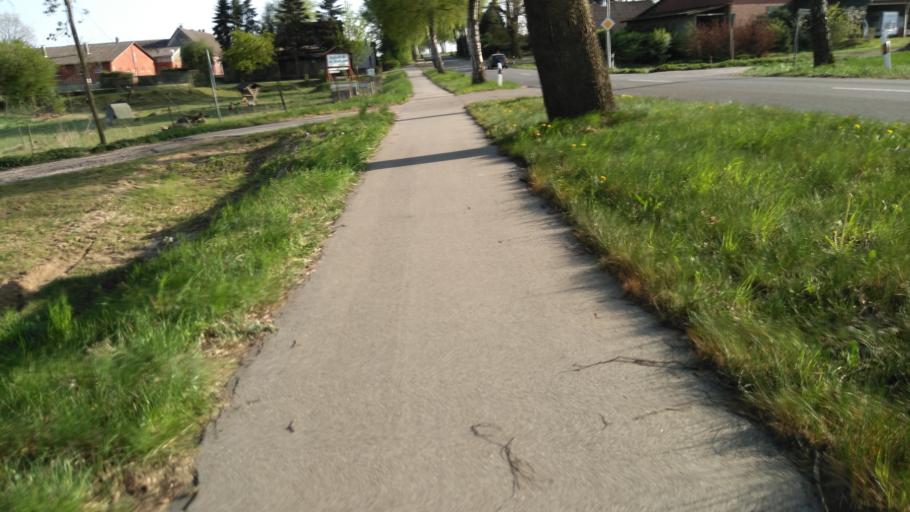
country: DE
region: Lower Saxony
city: Apensen
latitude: 53.4290
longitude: 9.6561
